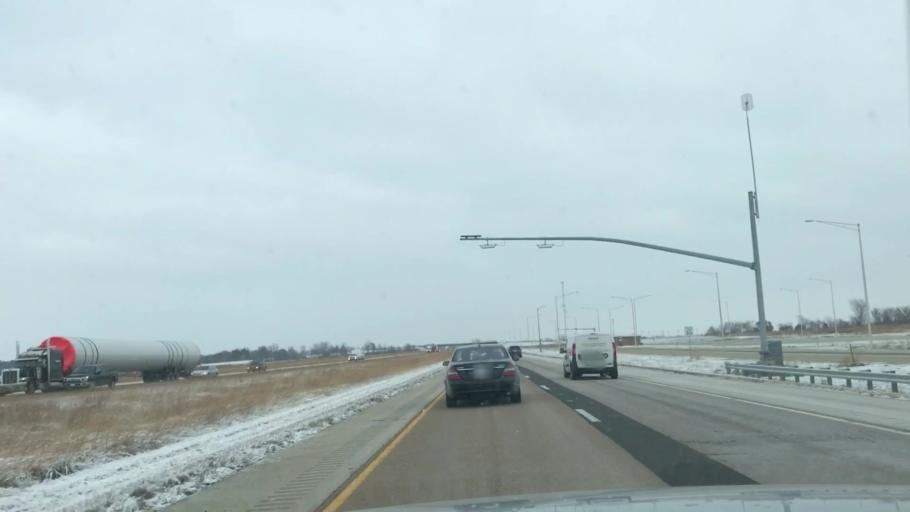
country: US
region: Illinois
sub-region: Montgomery County
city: Litchfield
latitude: 39.2254
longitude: -89.6452
